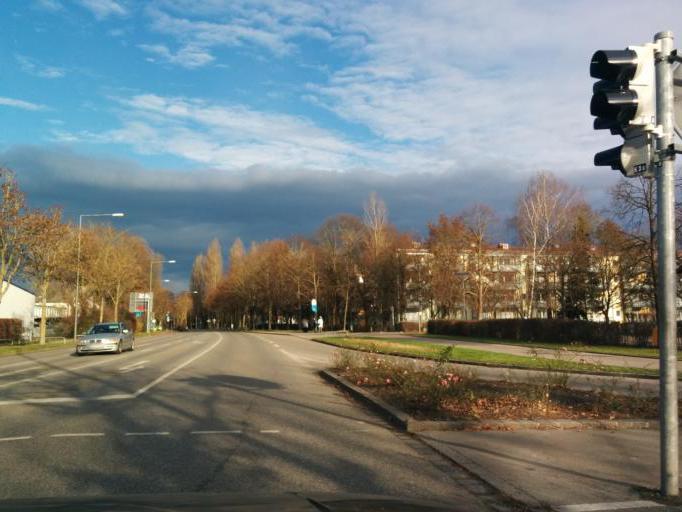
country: DE
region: Bavaria
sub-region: Upper Bavaria
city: Dachau
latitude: 48.2570
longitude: 11.4560
